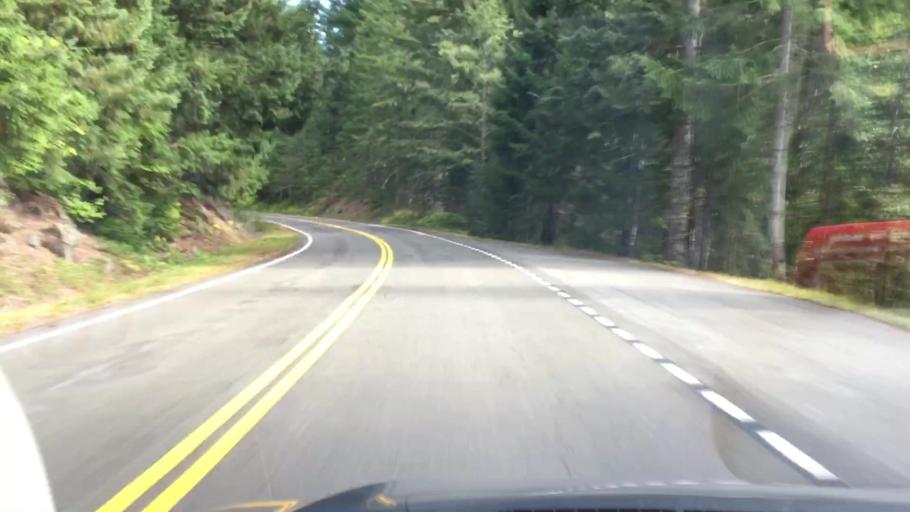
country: US
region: Washington
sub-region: Pierce County
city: Buckley
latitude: 46.7436
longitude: -121.6190
